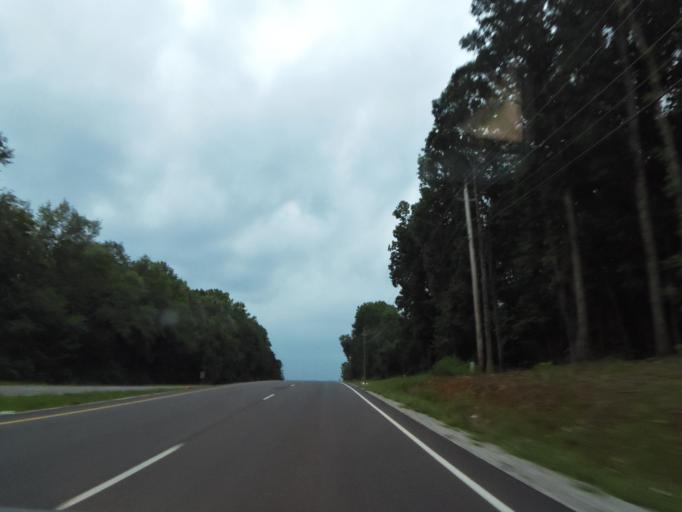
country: US
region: Alabama
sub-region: Madison County
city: Moores Mill
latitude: 34.7628
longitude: -86.4825
